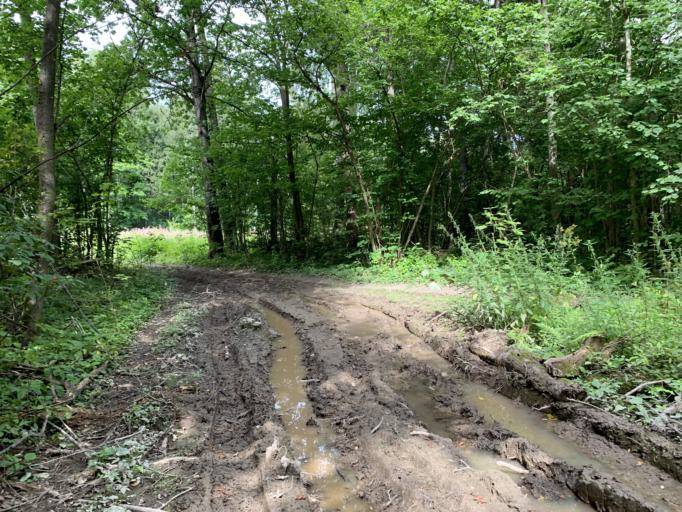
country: RU
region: Moskovskaya
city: Podosinki
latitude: 56.1815
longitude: 37.5678
